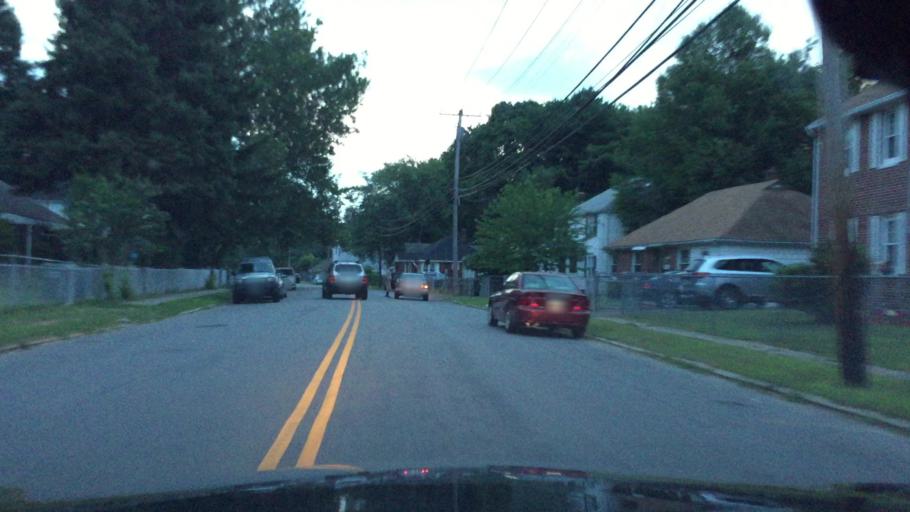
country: US
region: Connecticut
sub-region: Fairfield County
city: Stratford
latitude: 41.2019
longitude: -73.1610
